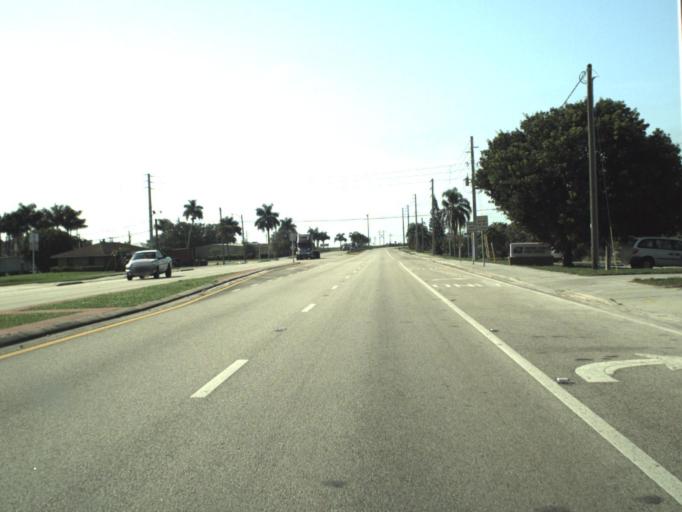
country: US
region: Florida
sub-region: Palm Beach County
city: South Bay
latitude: 26.6632
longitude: -80.7157
